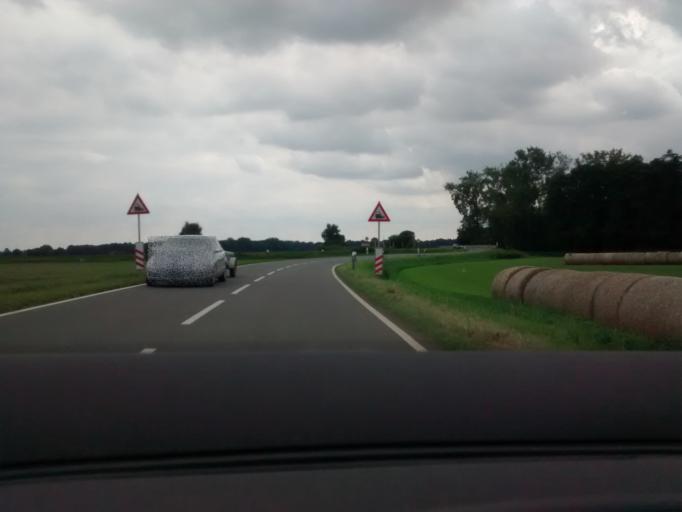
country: DE
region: Lower Saxony
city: Scharnebeck
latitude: 53.3203
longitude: 10.5054
